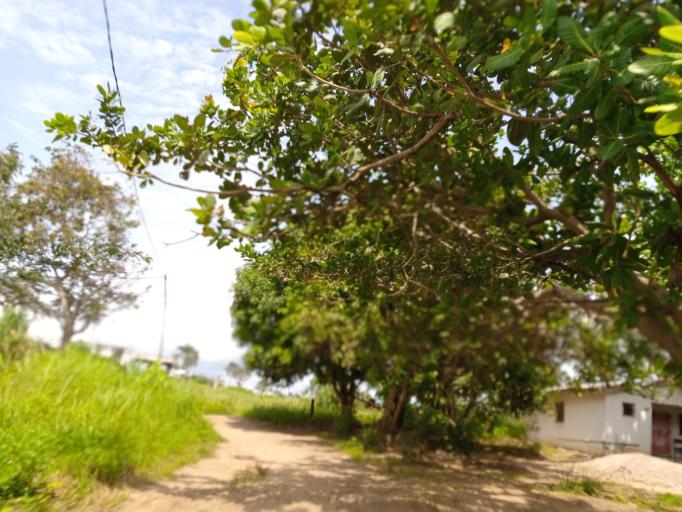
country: SL
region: Northern Province
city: Masoyila
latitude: 8.5339
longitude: -13.1473
